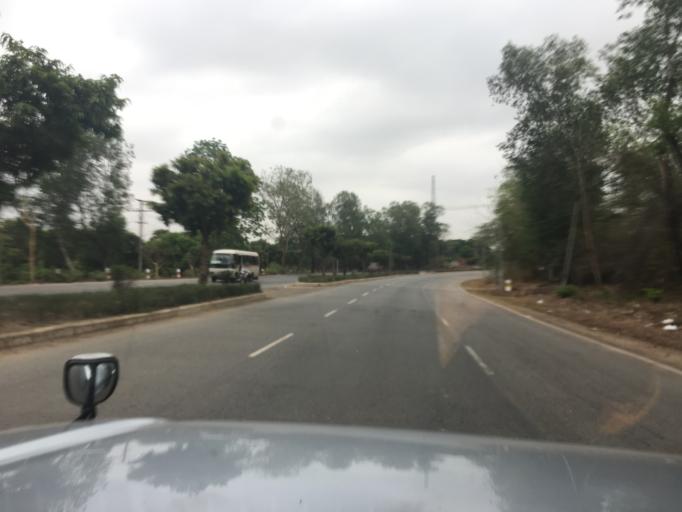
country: MM
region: Bago
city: Thanatpin
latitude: 17.2122
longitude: 96.4177
